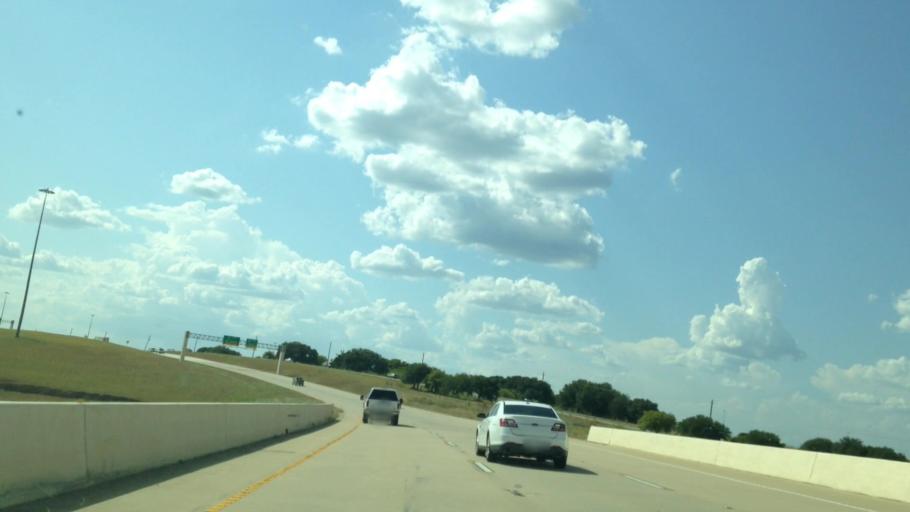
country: US
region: Texas
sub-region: Travis County
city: Onion Creek
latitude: 30.1107
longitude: -97.7950
